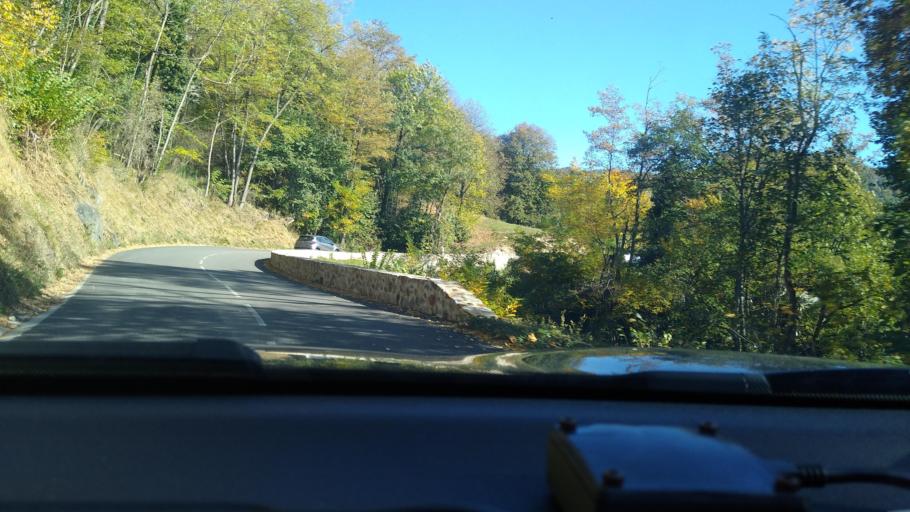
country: FR
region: Midi-Pyrenees
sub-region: Departement de l'Ariege
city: Ax-les-Thermes
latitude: 42.7226
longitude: 1.8424
